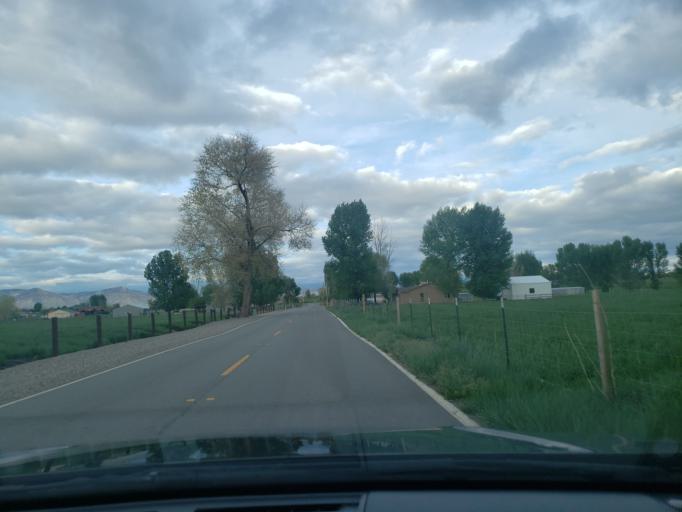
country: US
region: Colorado
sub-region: Mesa County
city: Fruita
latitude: 39.2112
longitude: -108.7241
